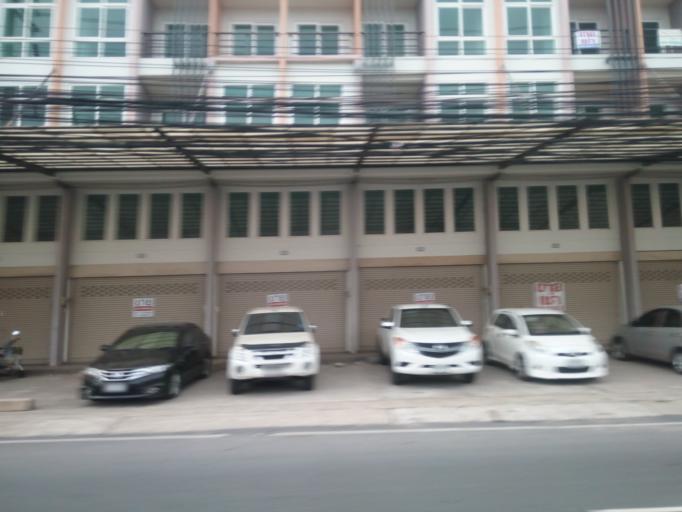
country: TH
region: Phuket
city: Ban Talat Nua
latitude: 7.8850
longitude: 98.3644
